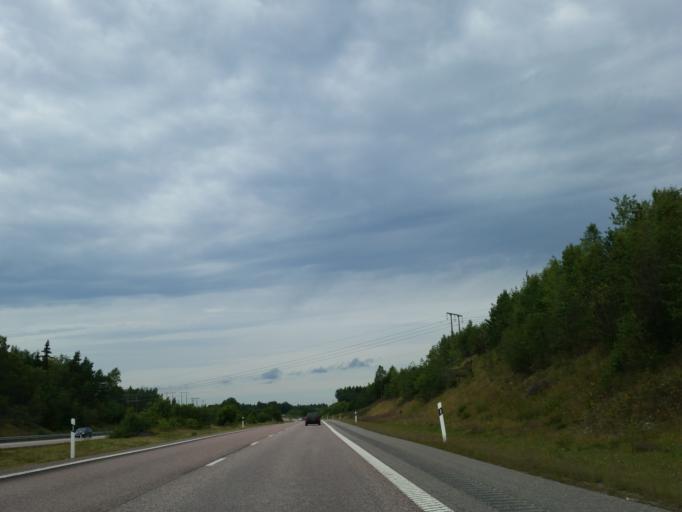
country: SE
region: Stockholm
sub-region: Nykvarns Kommun
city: Nykvarn
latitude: 59.2027
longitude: 17.3624
